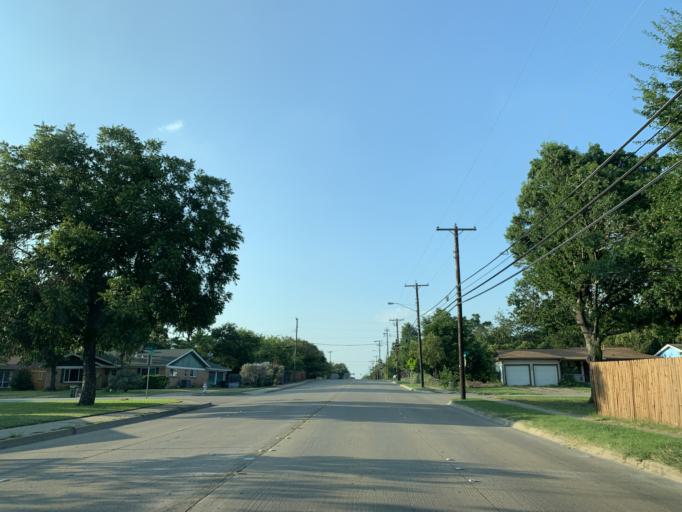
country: US
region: Texas
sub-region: Tarrant County
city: Hurst
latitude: 32.8148
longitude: -97.1865
